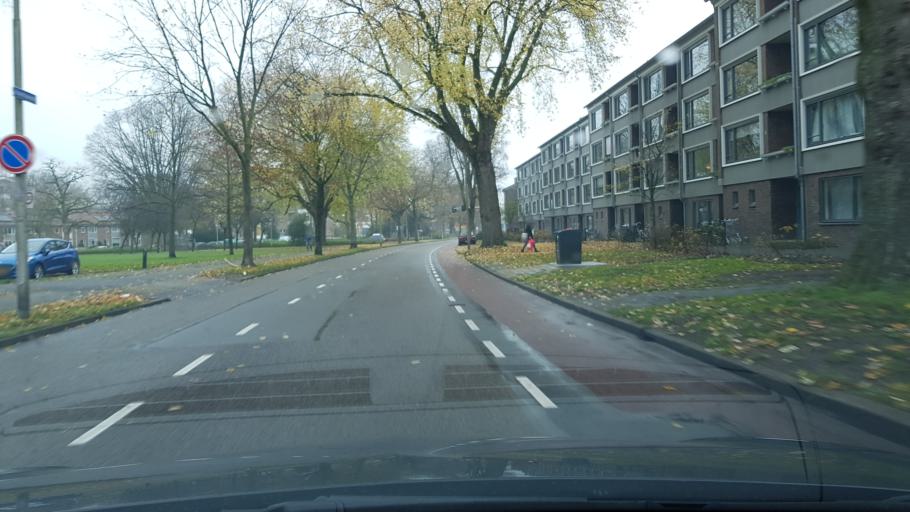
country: NL
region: Utrecht
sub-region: Gemeente Amersfoort
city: Hoogland
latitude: 52.1619
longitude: 5.3577
